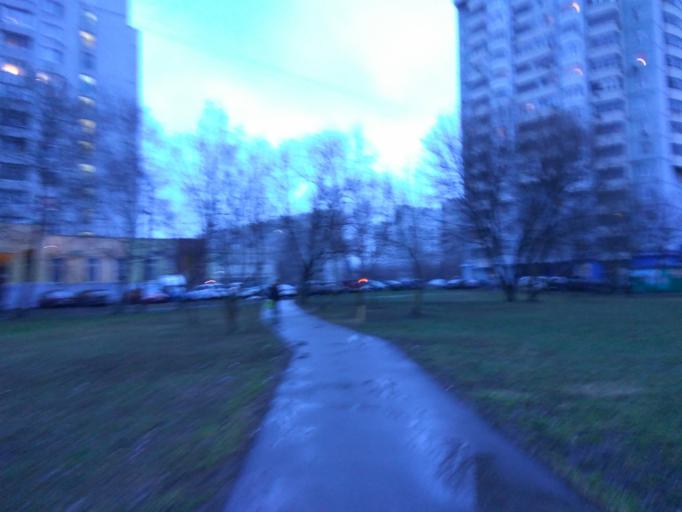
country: RU
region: Moscow
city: Lianozovo
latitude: 55.9025
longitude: 37.5718
